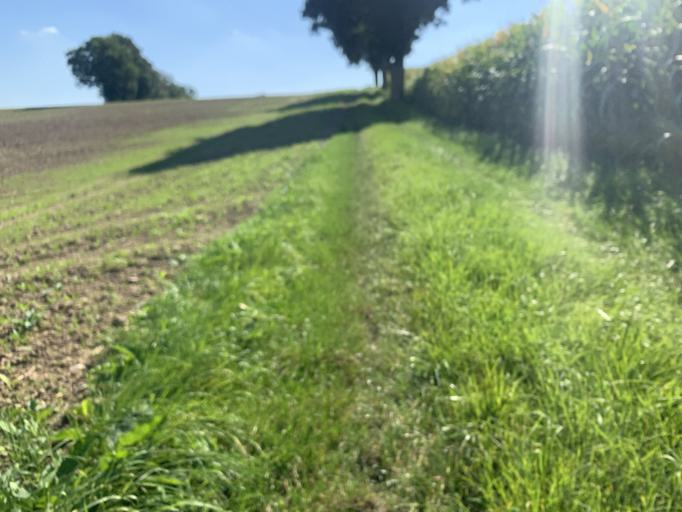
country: DE
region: Bavaria
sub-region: Swabia
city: Mering
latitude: 48.2833
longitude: 11.0053
